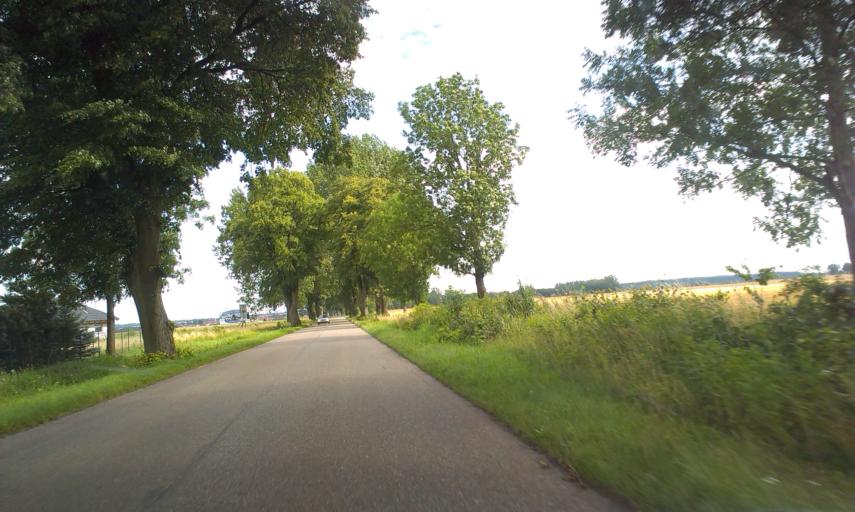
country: PL
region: Greater Poland Voivodeship
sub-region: Powiat zlotowski
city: Zlotow
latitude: 53.3859
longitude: 17.0141
